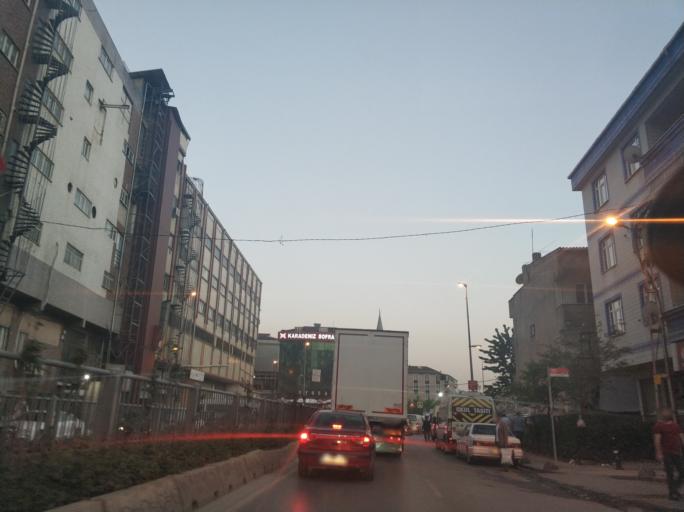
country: TR
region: Istanbul
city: Bagcilar
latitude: 41.0545
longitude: 28.8488
